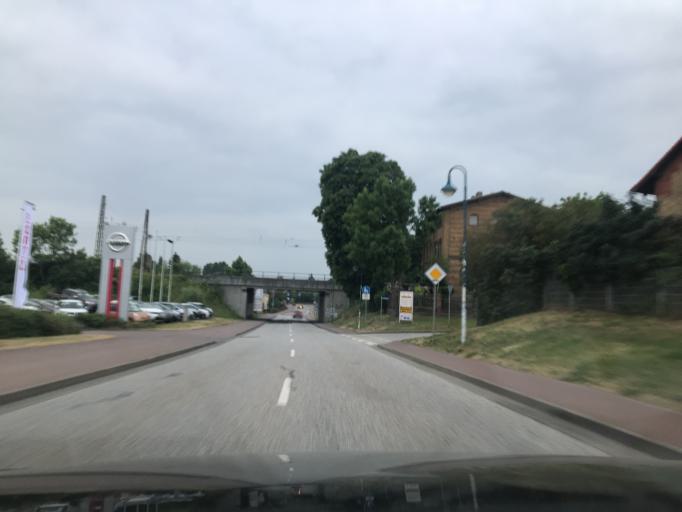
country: DE
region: Saxony-Anhalt
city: Angersdorf
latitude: 51.4604
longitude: 11.9083
